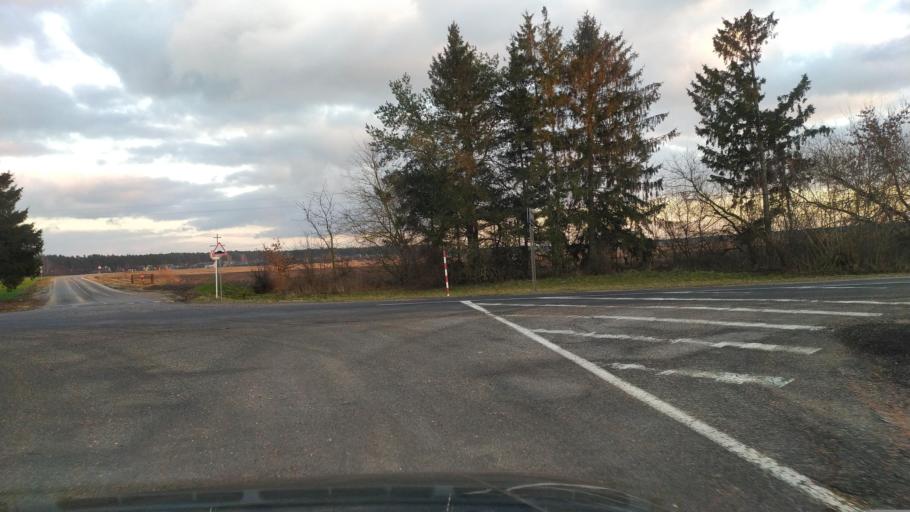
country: BY
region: Brest
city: Kamyanyets
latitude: 52.3705
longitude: 23.7931
